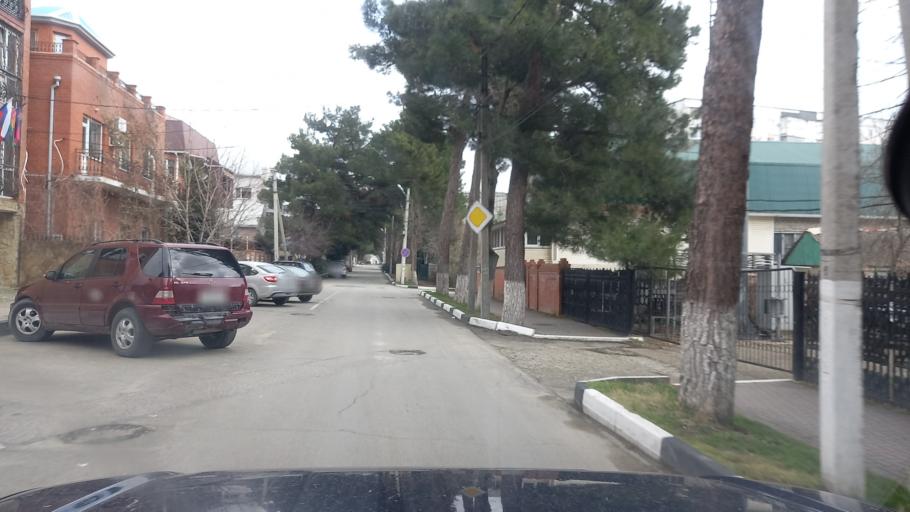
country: RU
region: Krasnodarskiy
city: Gelendzhik
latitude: 44.5604
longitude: 38.0853
